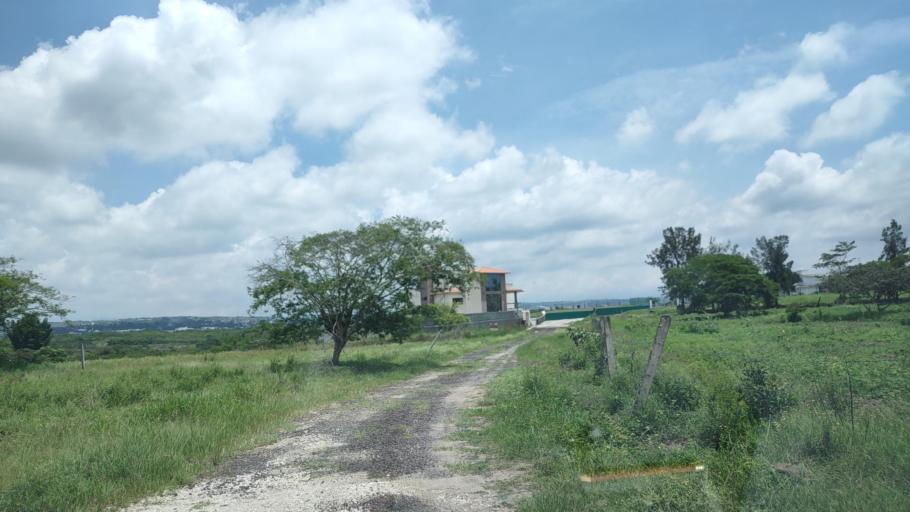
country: MX
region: Veracruz
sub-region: Emiliano Zapata
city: Dos Rios
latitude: 19.4671
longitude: -96.7922
